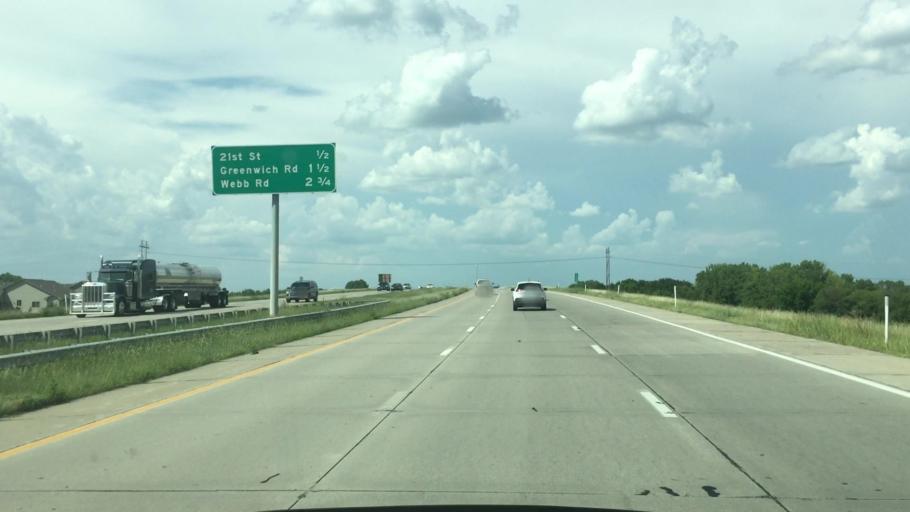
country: US
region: Kansas
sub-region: Butler County
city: Andover
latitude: 37.7127
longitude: -97.1997
